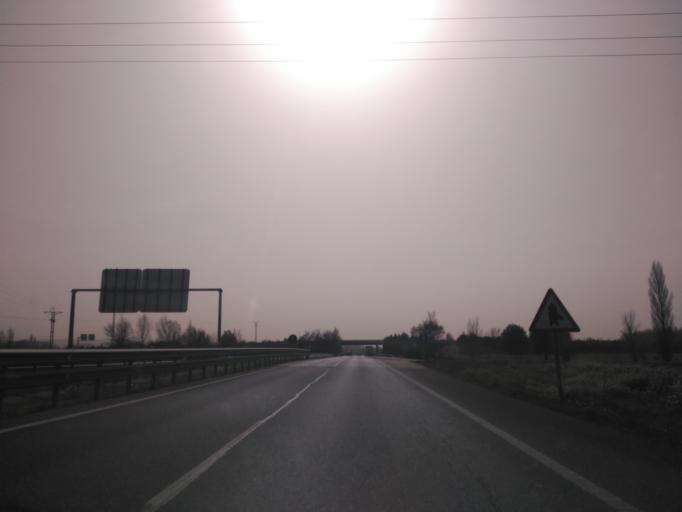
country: ES
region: Castille and Leon
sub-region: Provincia de Palencia
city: Villamuriel de Cerrato
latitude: 41.9414
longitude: -4.5036
